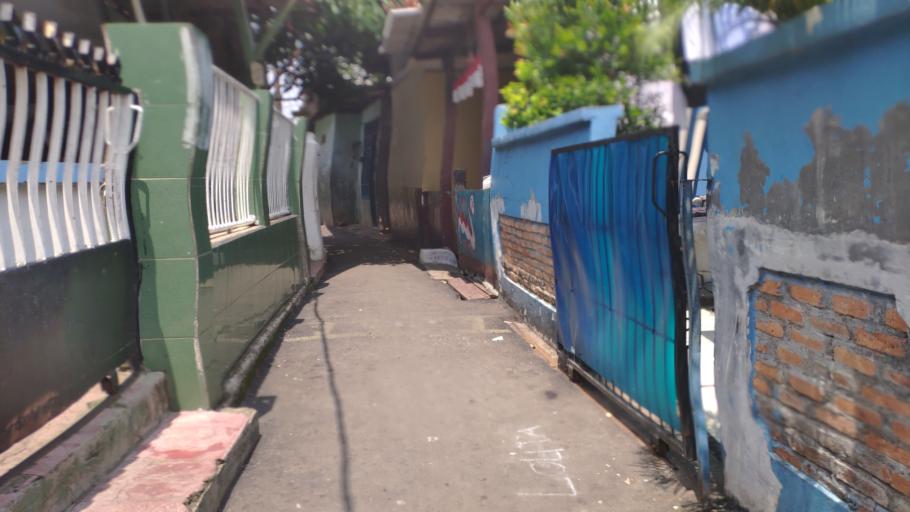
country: ID
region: Jakarta Raya
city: Jakarta
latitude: -6.2687
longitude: 106.8282
